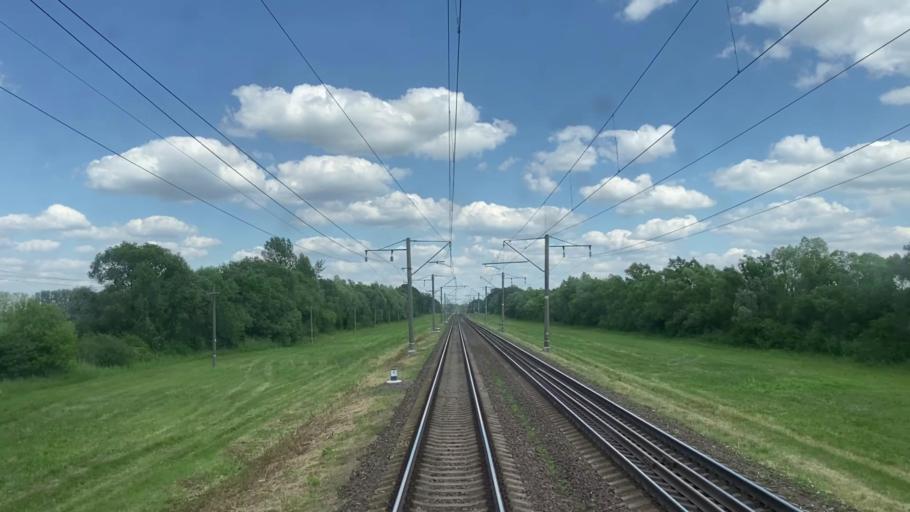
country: BY
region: Brest
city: Zhabinka
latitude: 52.2616
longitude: 24.1377
